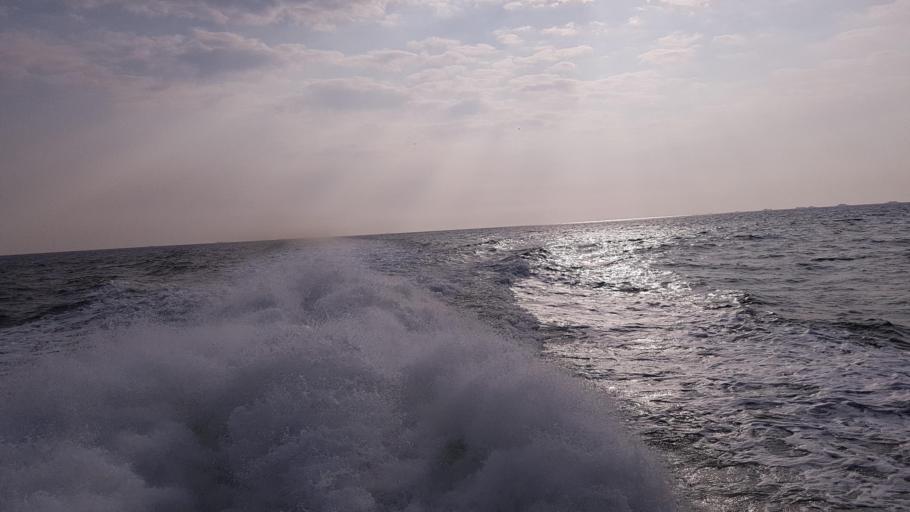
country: DE
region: Schleswig-Holstein
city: Grode
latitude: 54.6174
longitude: 8.7196
